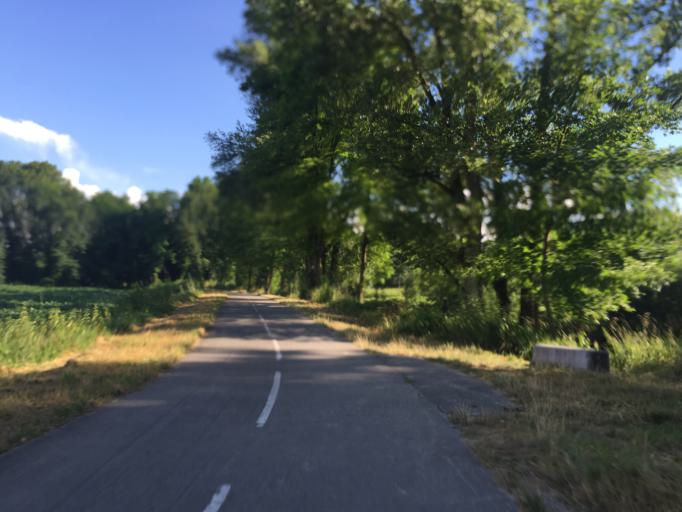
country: FR
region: Rhone-Alpes
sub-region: Departement de la Savoie
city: Le Bourget-du-Lac
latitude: 45.6270
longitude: 5.8733
